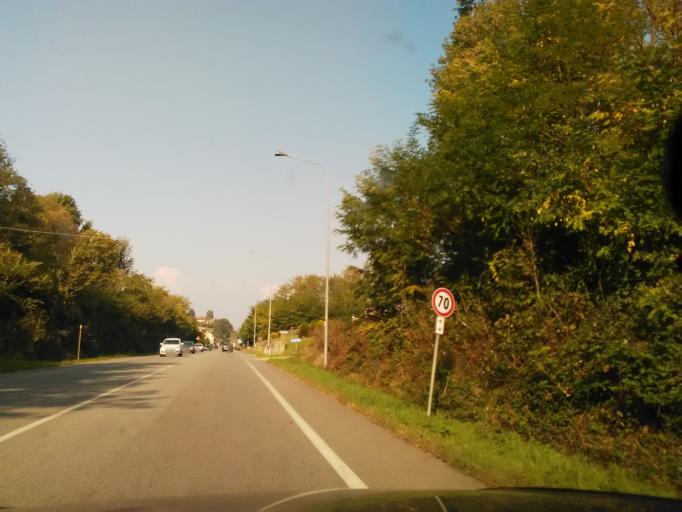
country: IT
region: Piedmont
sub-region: Provincia di Biella
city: Salussola
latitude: 45.4407
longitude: 8.1123
